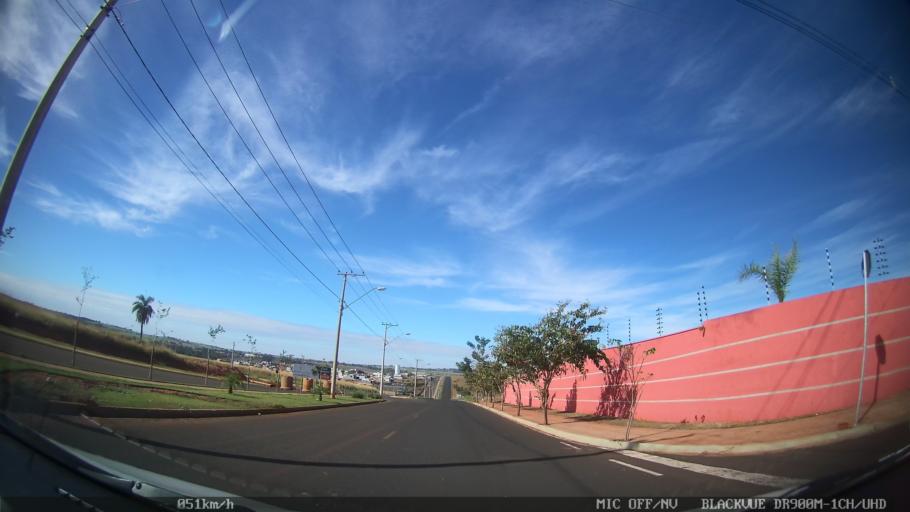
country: BR
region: Sao Paulo
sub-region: Sao Jose Do Rio Preto
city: Sao Jose do Rio Preto
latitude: -20.8055
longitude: -49.3269
